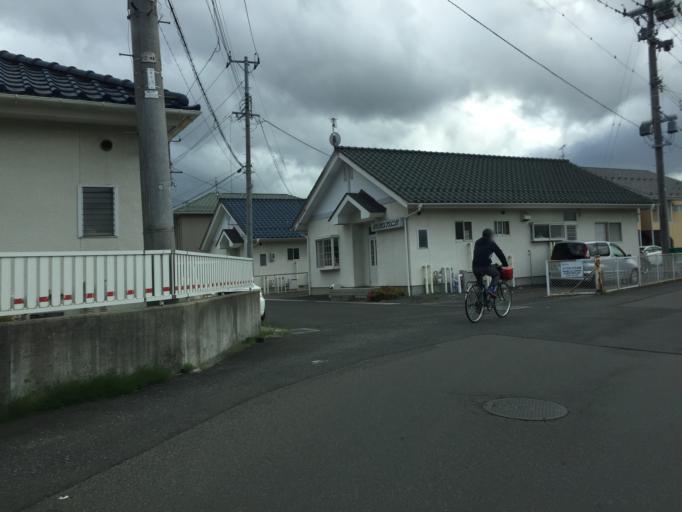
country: JP
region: Fukushima
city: Fukushima-shi
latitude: 37.7712
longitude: 140.4530
